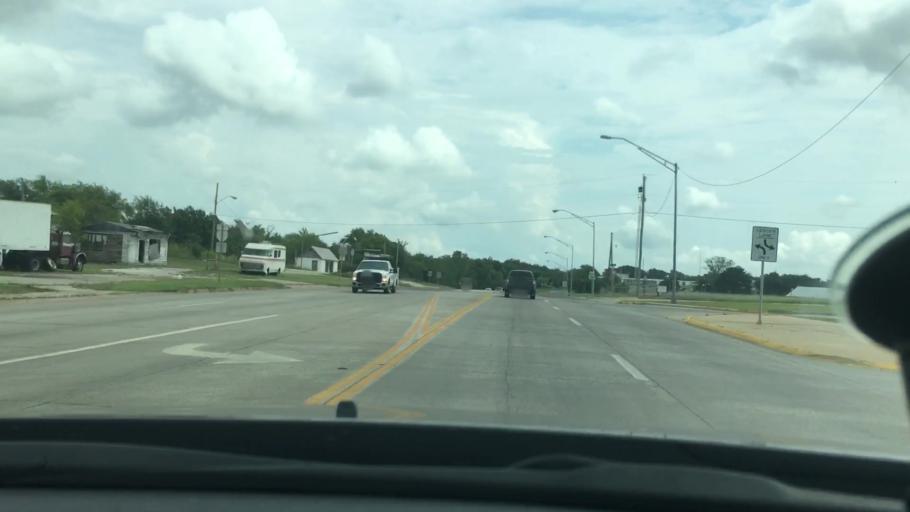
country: US
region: Oklahoma
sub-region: Carter County
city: Ardmore
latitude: 34.1855
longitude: -97.1079
